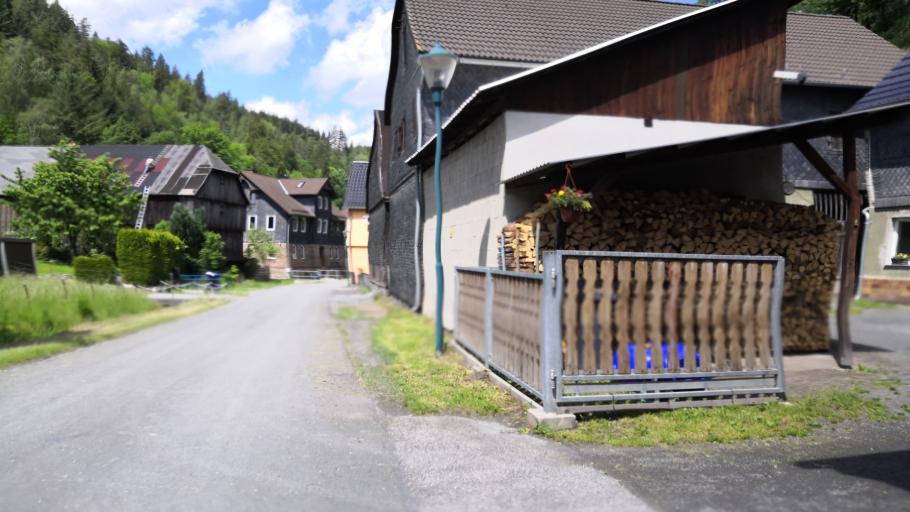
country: DE
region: Thuringia
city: Probstzella
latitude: 50.5652
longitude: 11.3790
